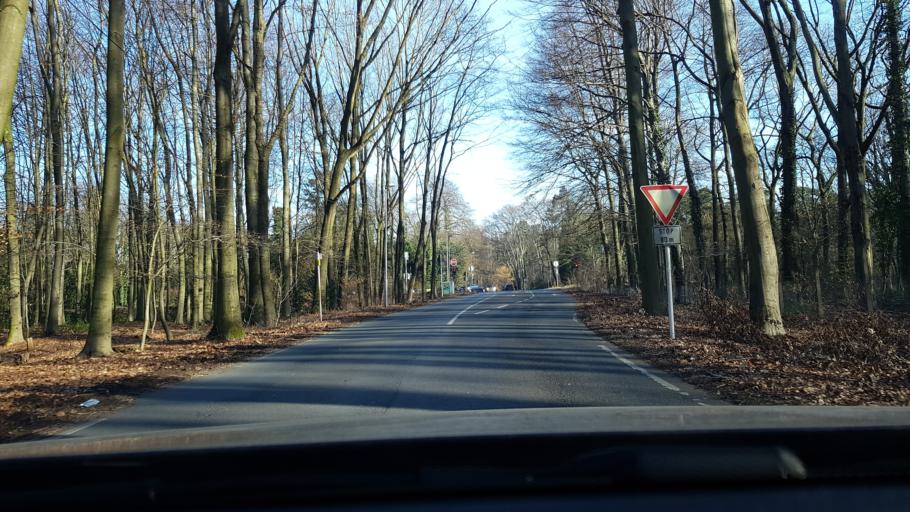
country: DE
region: North Rhine-Westphalia
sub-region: Regierungsbezirk Dusseldorf
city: Duisburg
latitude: 51.4106
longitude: 6.8220
